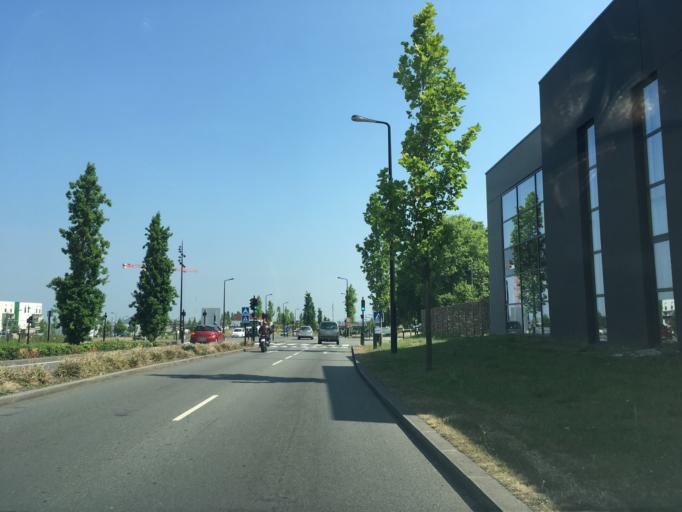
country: FR
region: Nord-Pas-de-Calais
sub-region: Departement du Nord
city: Aulnoy-lez-Valenciennes
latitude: 50.3397
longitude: 3.5139
